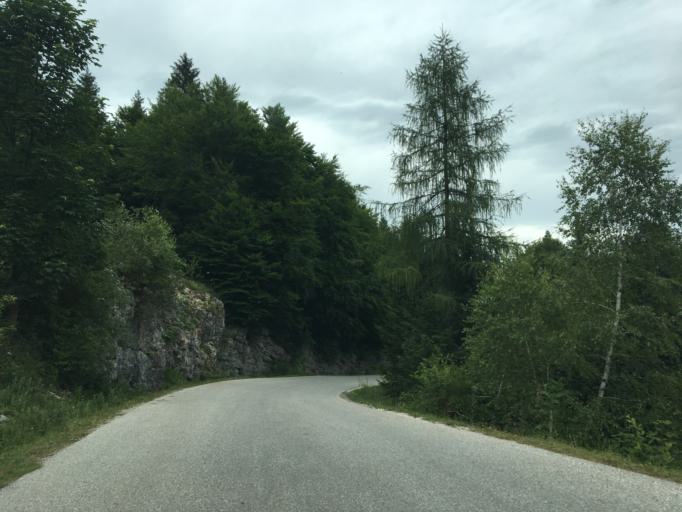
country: AT
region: Salzburg
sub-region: Politischer Bezirk Salzburg-Umgebung
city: Strobl
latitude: 47.6609
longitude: 13.4557
